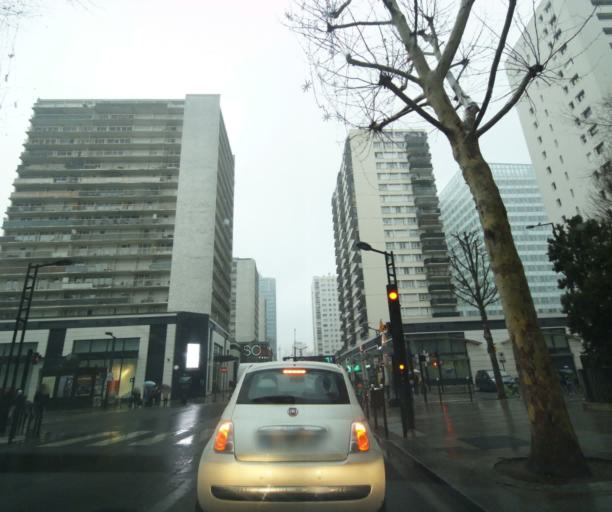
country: FR
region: Ile-de-France
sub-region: Departement des Hauts-de-Seine
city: Levallois-Perret
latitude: 48.8907
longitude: 2.2945
